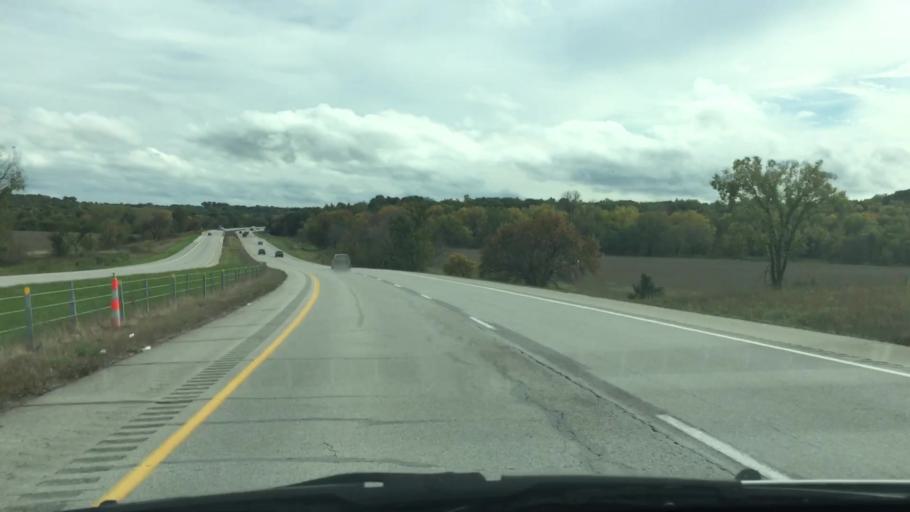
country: US
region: Iowa
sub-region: Clarke County
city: Osceola
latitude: 41.1102
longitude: -93.7815
